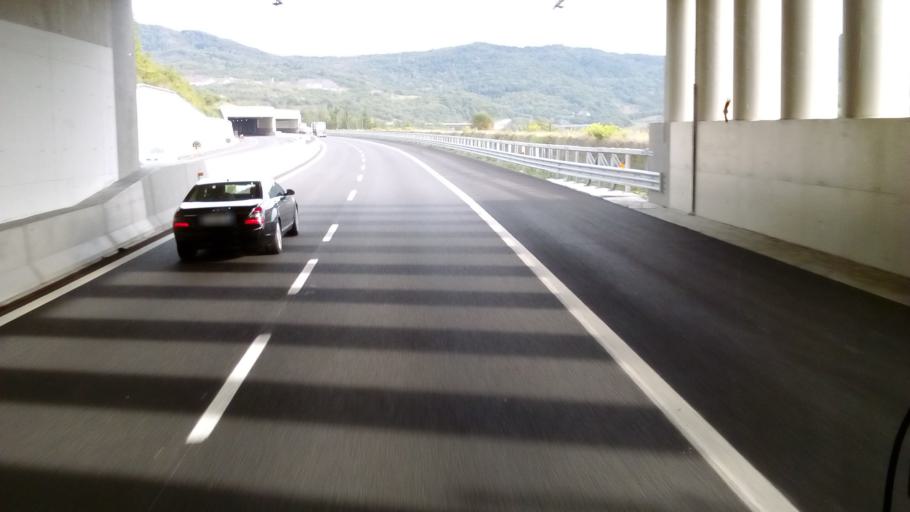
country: IT
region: Tuscany
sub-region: Province of Florence
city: Barberino di Mugello
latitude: 44.0567
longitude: 11.2445
